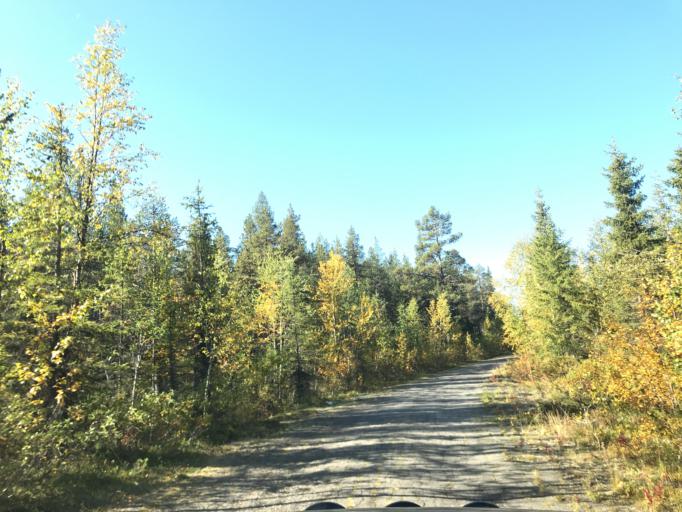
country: SE
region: Norrbotten
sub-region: Gallivare Kommun
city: Malmberget
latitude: 67.6459
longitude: 21.0805
